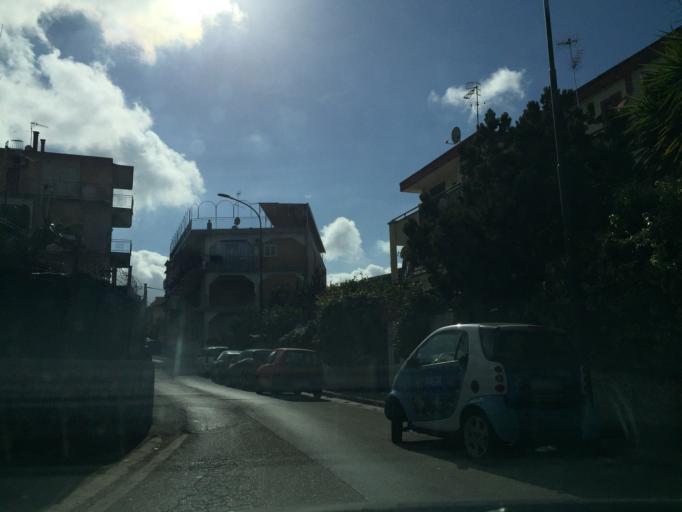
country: IT
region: Campania
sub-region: Provincia di Napoli
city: Massa di Somma
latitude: 40.8492
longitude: 14.3695
